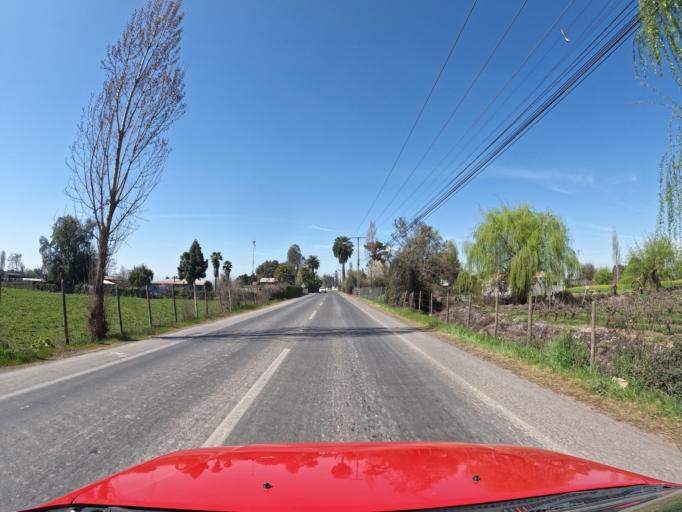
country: CL
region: Maule
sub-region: Provincia de Curico
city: Rauco
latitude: -35.0010
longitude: -71.3348
